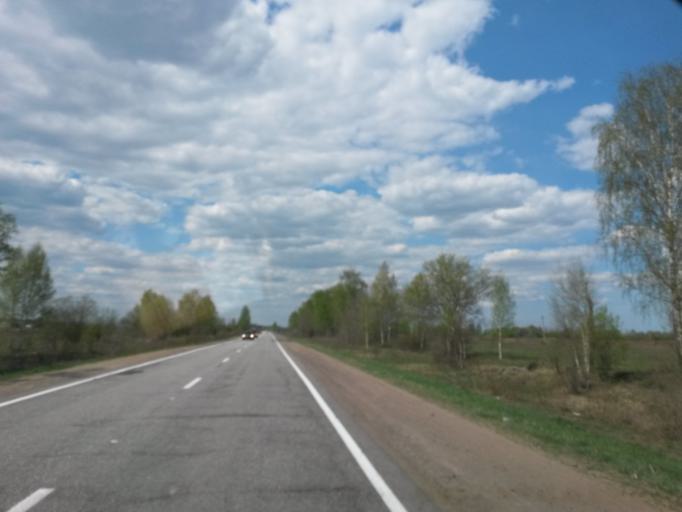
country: RU
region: Jaroslavl
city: Konstantinovskiy
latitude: 57.6687
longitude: 39.6296
